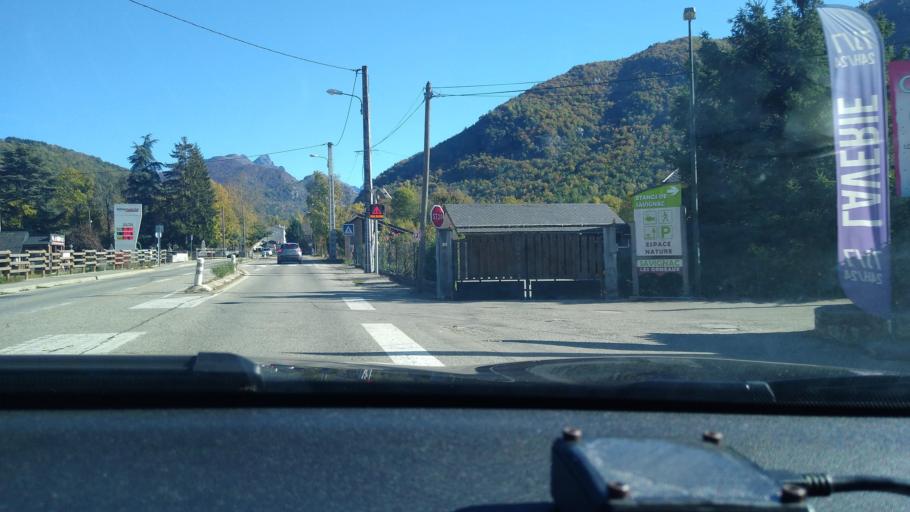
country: FR
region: Midi-Pyrenees
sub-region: Departement de l'Ariege
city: Ax-les-Thermes
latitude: 42.7300
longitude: 1.8139
